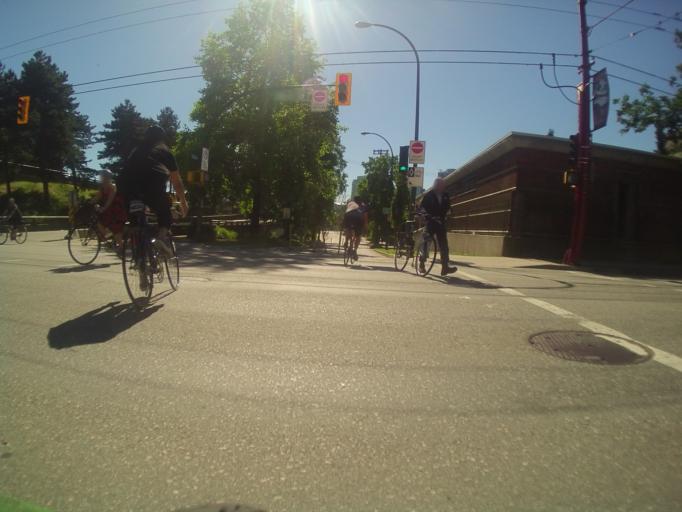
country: CA
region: British Columbia
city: West End
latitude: 49.2777
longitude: -123.0997
